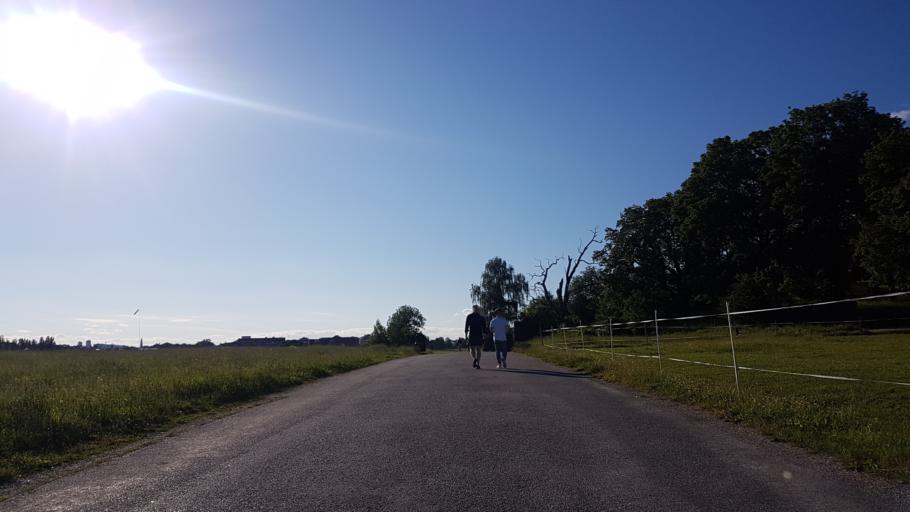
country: SE
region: Stockholm
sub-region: Stockholms Kommun
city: OEstermalm
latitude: 59.3369
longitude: 18.1165
